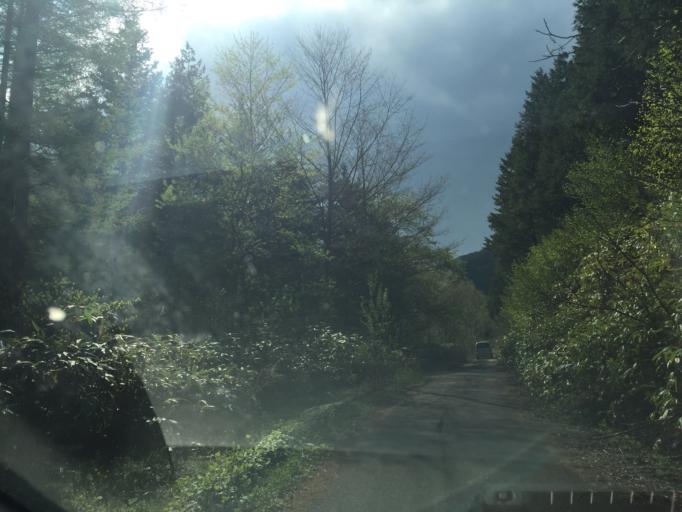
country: JP
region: Nagano
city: Iida
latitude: 35.5123
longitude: 137.6614
